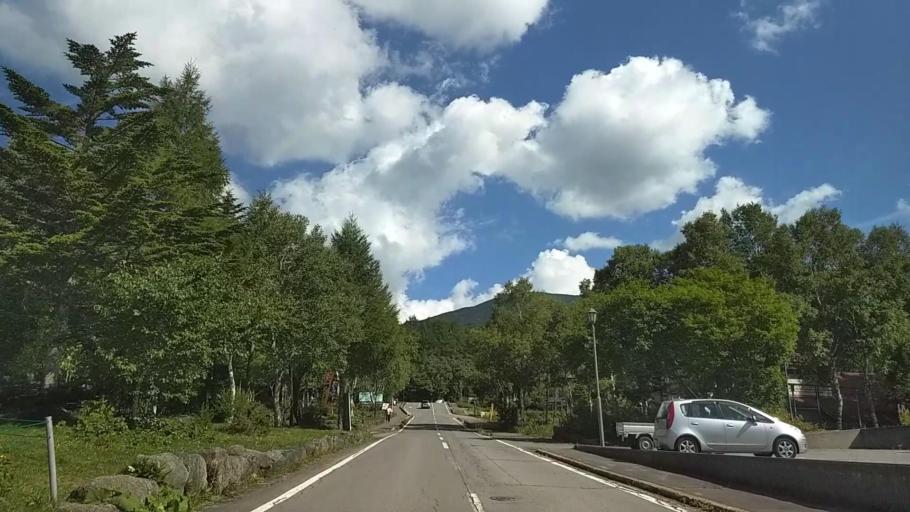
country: JP
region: Nagano
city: Chino
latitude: 36.1340
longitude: 138.2692
